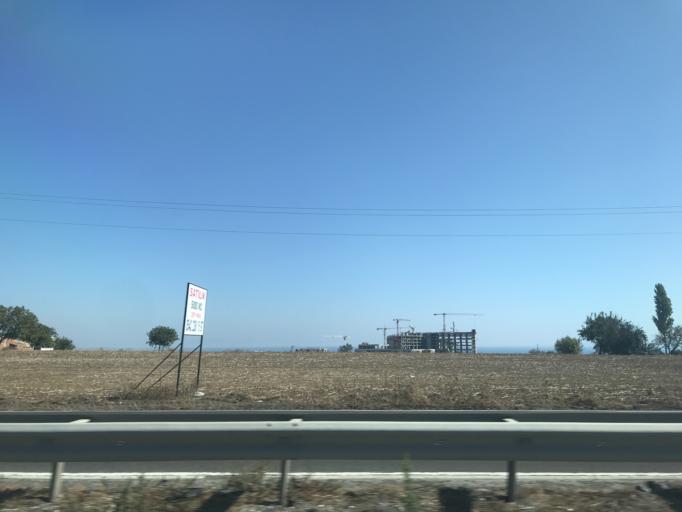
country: TR
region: Tekirdag
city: Tekirdag
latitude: 41.0117
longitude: 27.5156
